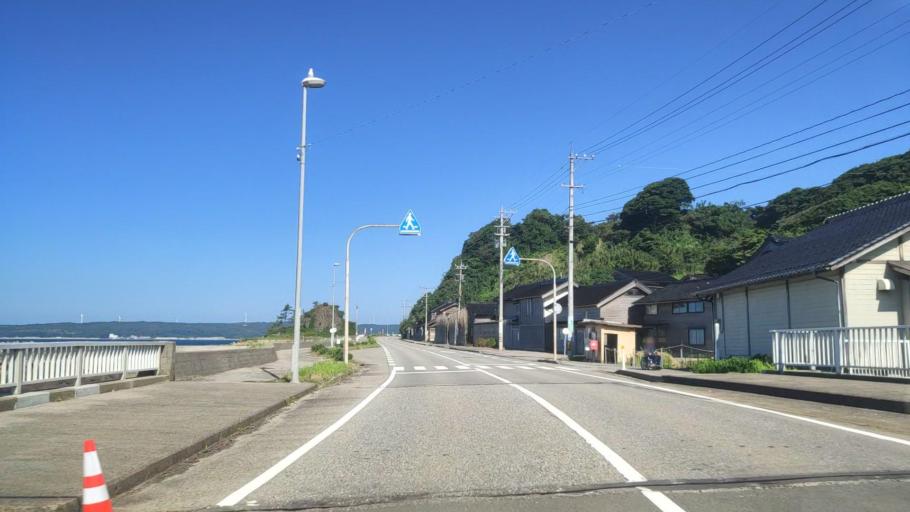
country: JP
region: Ishikawa
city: Hakui
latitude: 37.1268
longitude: 136.7292
